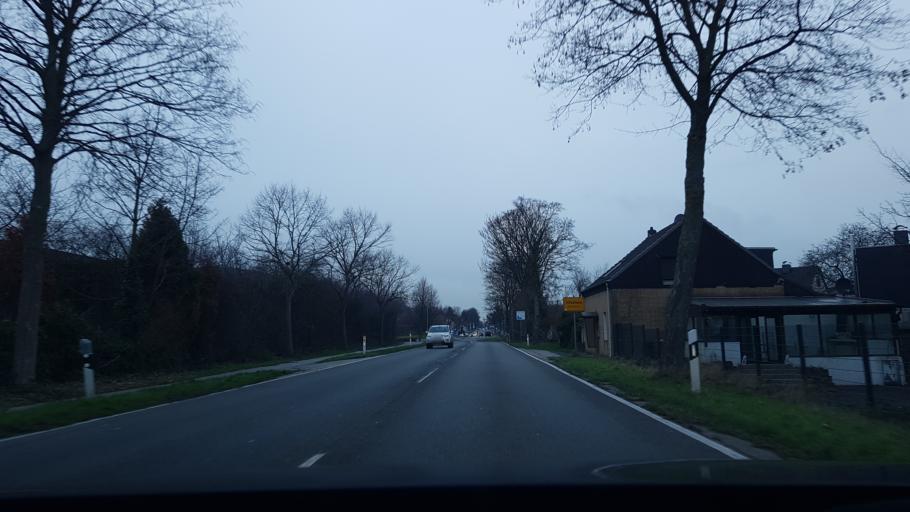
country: DE
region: North Rhine-Westphalia
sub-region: Regierungsbezirk Dusseldorf
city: Moers
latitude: 51.4181
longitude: 6.6569
